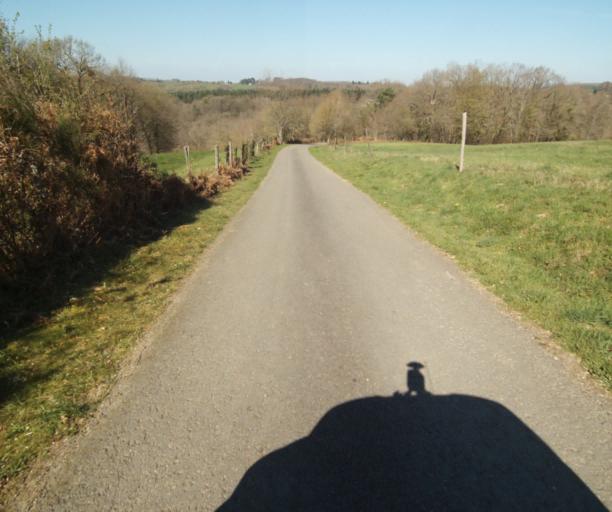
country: FR
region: Limousin
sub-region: Departement de la Correze
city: Saint-Mexant
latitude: 45.3160
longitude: 1.6074
